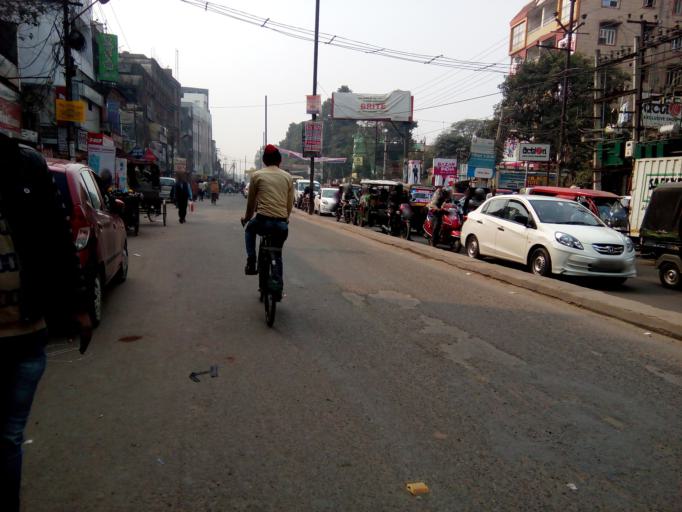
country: IN
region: Bihar
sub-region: Patna
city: Patna
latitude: 25.6191
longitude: 85.1527
